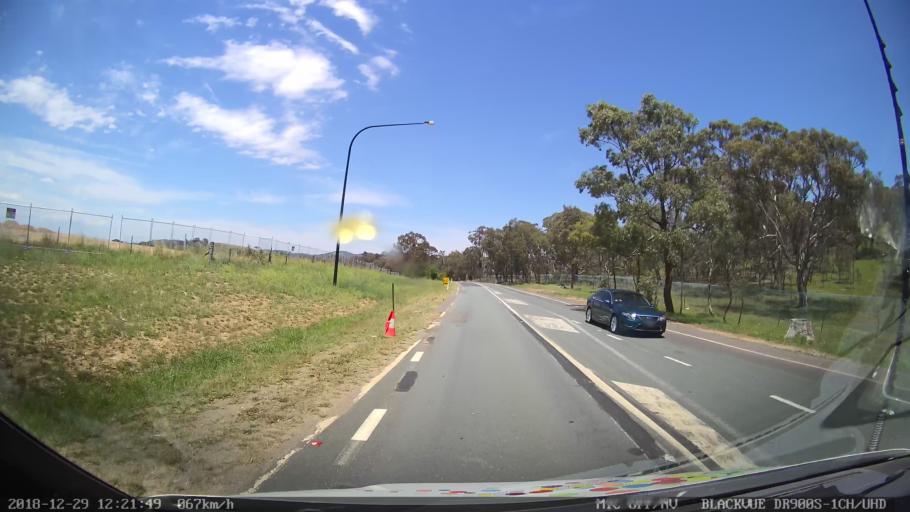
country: AU
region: New South Wales
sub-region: Queanbeyan
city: Queanbeyan
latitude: -35.4175
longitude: 149.2216
